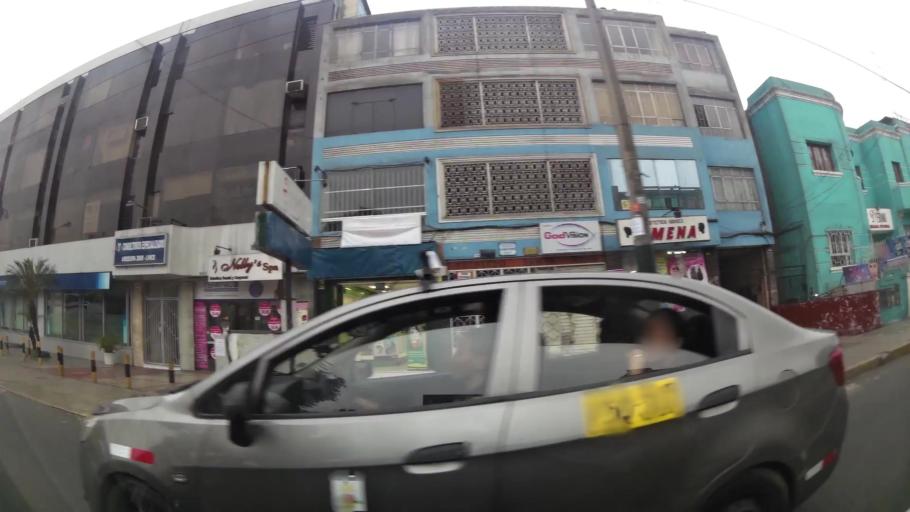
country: PE
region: Lima
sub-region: Lima
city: San Isidro
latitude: -12.0853
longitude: -77.0344
